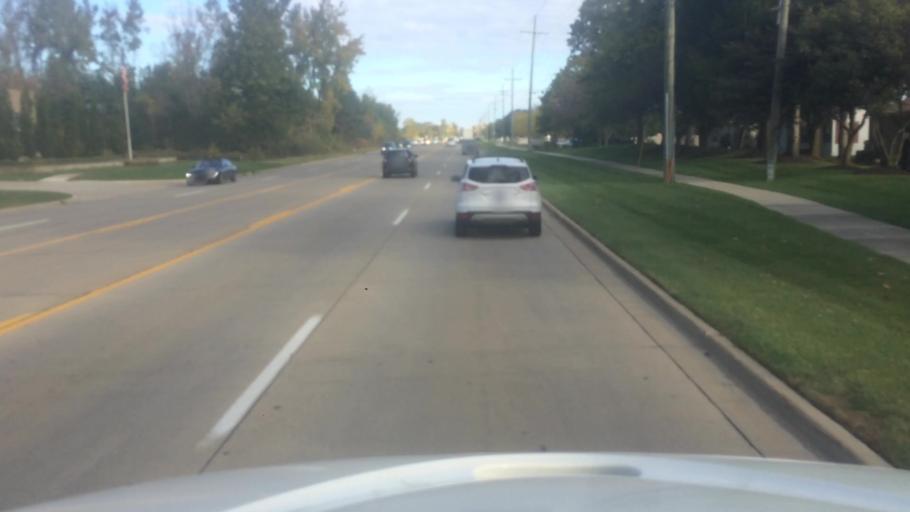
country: US
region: Michigan
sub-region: Macomb County
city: Shelby
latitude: 42.6638
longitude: -82.9943
